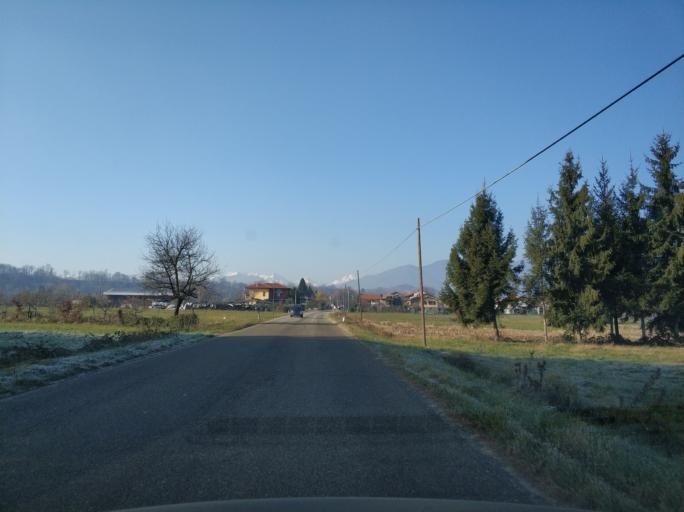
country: IT
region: Piedmont
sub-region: Provincia di Torino
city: Levone
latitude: 45.2989
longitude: 7.6057
